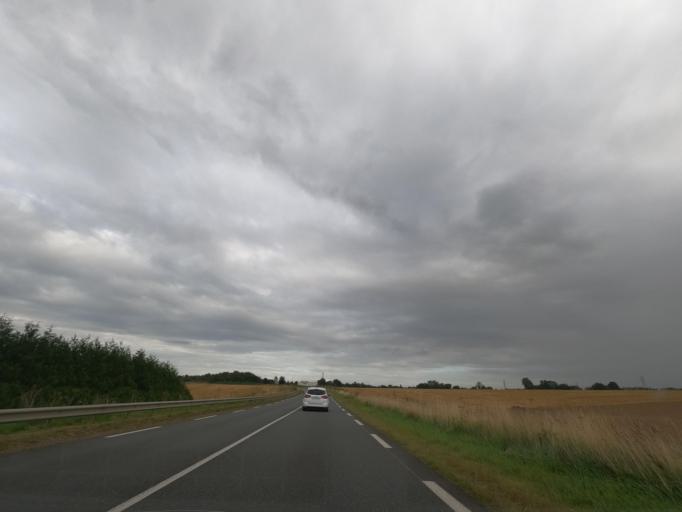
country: FR
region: Haute-Normandie
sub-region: Departement de l'Eure
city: Bourgtheroulde-Infreville
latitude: 49.2923
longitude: 0.8693
